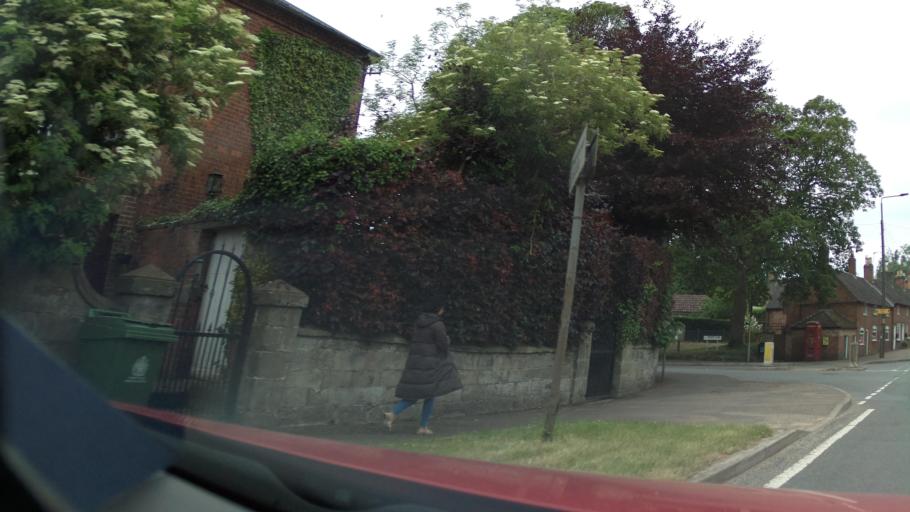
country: GB
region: England
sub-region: Derbyshire
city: Etwall
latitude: 52.9462
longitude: -1.5711
